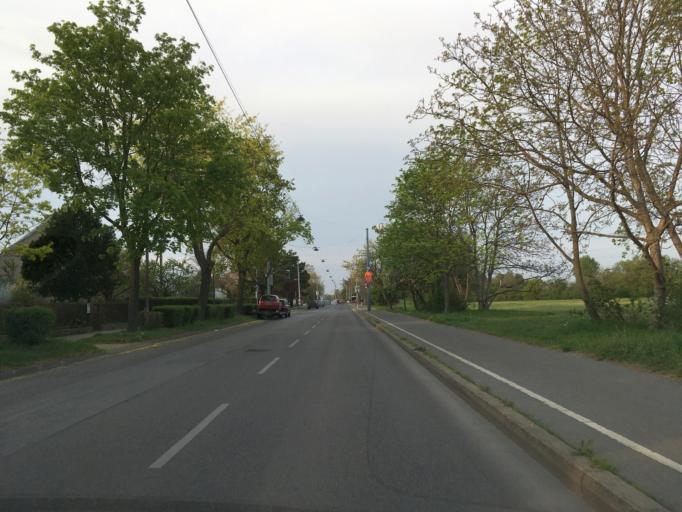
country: AT
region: Lower Austria
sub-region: Politischer Bezirk Wien-Umgebung
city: Gerasdorf bei Wien
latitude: 48.2790
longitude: 16.4245
